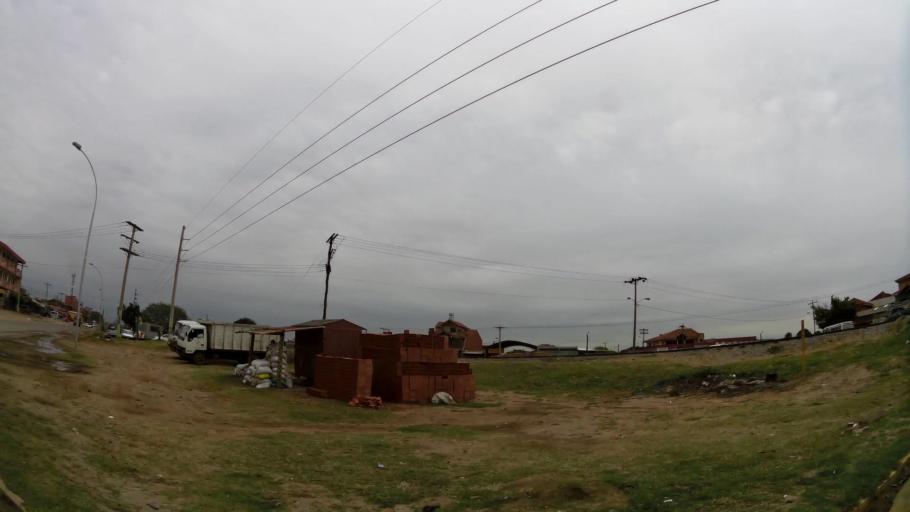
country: BO
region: Santa Cruz
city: Santa Cruz de la Sierra
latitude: -17.8412
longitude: -63.1716
